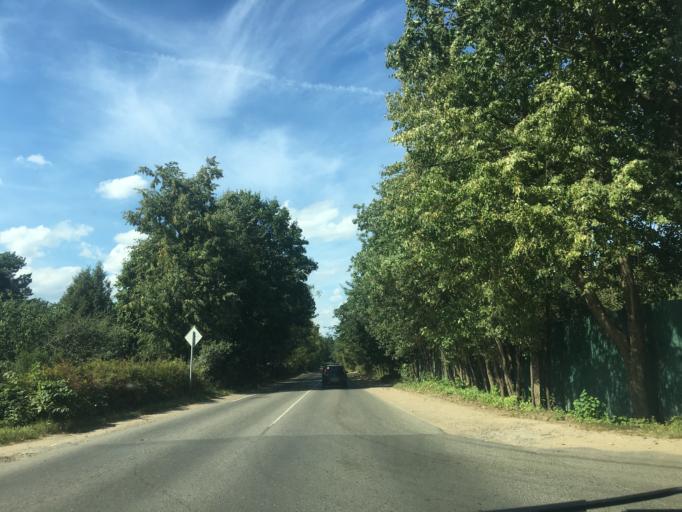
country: RU
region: Moskovskaya
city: Vidnoye
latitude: 55.5159
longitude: 37.6832
